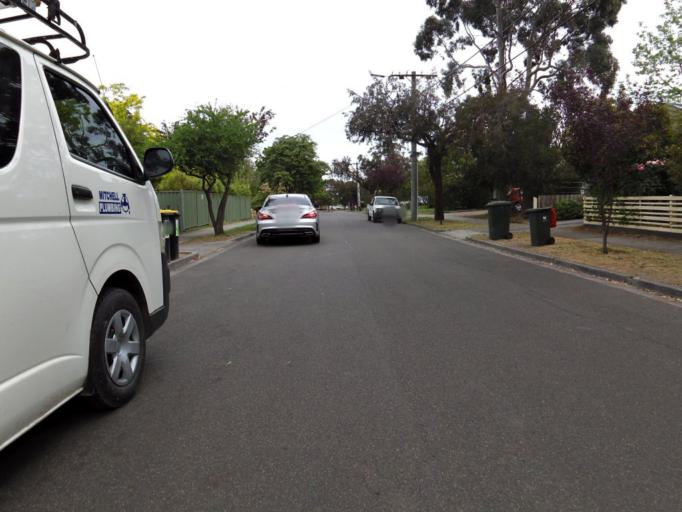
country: AU
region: Victoria
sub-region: Monash
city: Clayton
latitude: -37.9124
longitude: 145.1277
